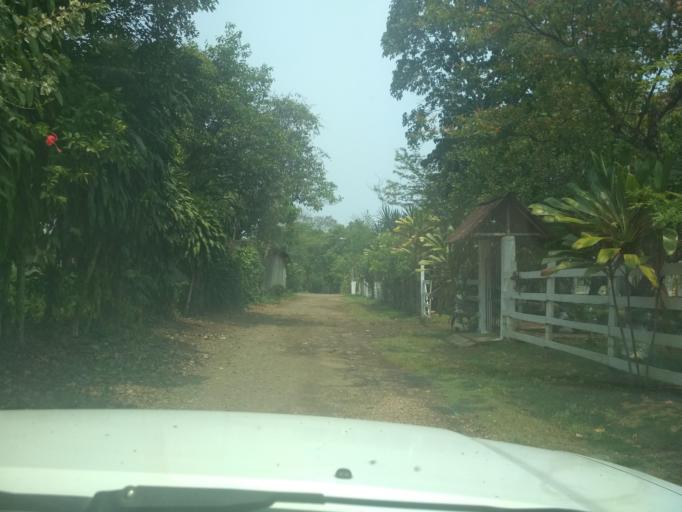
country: MX
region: Veracruz
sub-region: Tezonapa
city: Laguna Chica (Pueblo Nuevo)
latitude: 18.5168
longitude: -96.7776
